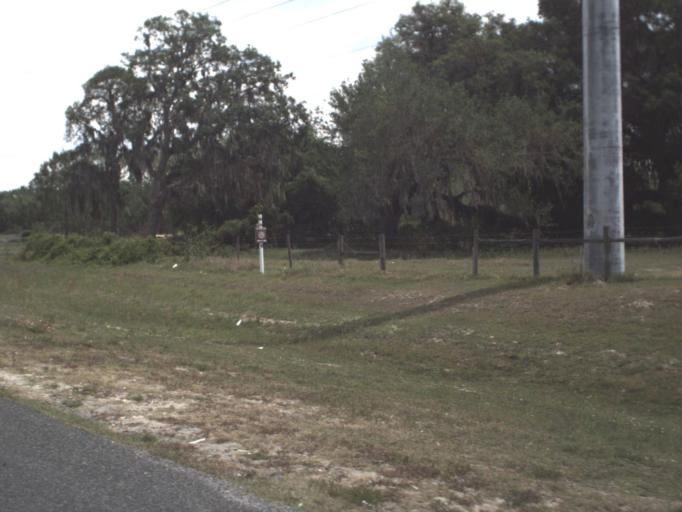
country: US
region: Florida
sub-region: Sumter County
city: Wildwood
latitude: 28.8239
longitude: -81.9740
